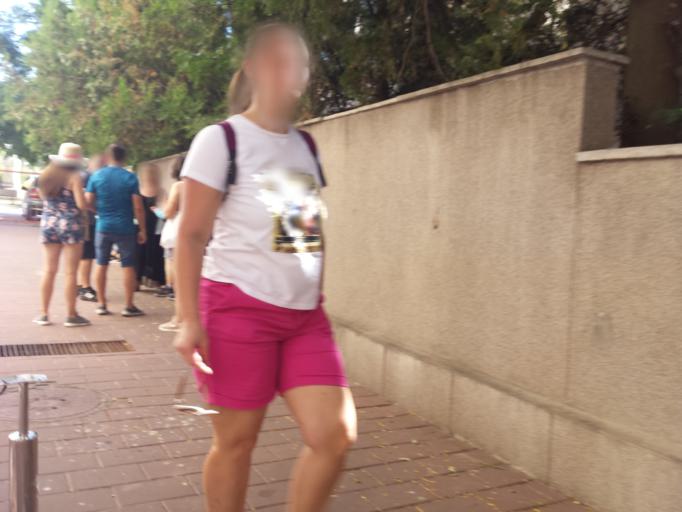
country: RO
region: Tulcea
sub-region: Municipiul Tulcea
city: Tulcea
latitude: 45.1801
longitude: 28.8054
